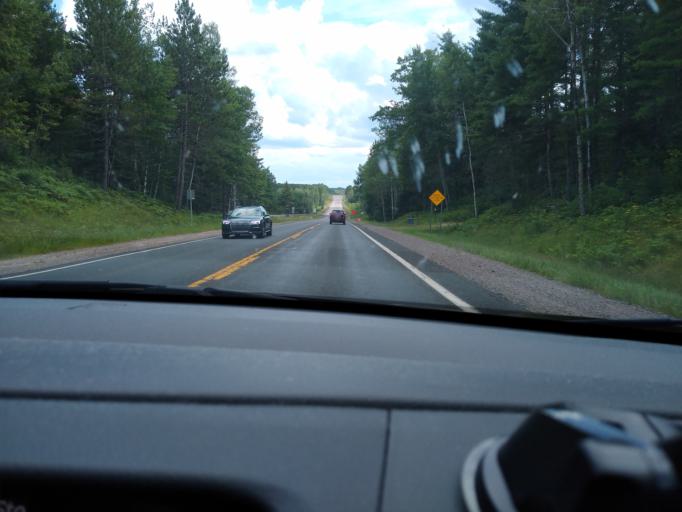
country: US
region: Michigan
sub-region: Iron County
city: Crystal Falls
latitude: 46.2510
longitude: -88.0112
